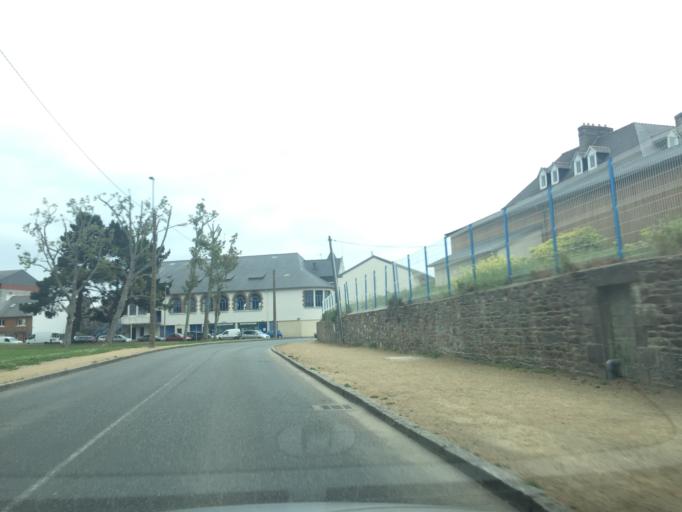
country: FR
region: Brittany
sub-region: Departement des Cotes-d'Armor
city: Paimpol
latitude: 48.7825
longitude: -3.0466
